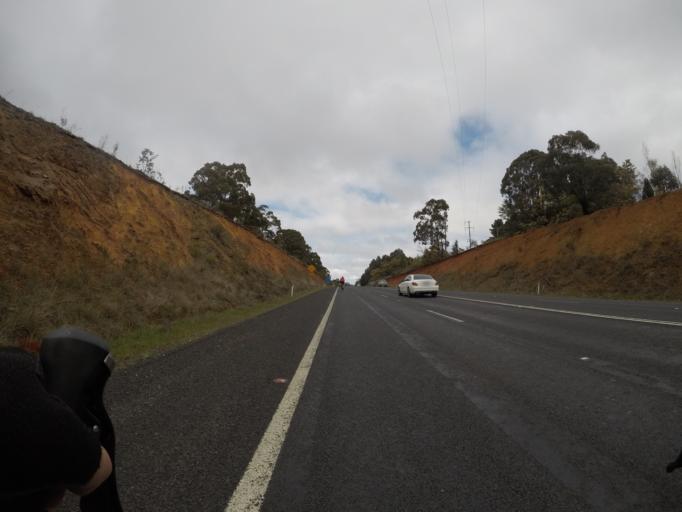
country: AU
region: New South Wales
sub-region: Lithgow
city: Portland
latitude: -33.4419
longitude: 149.8364
